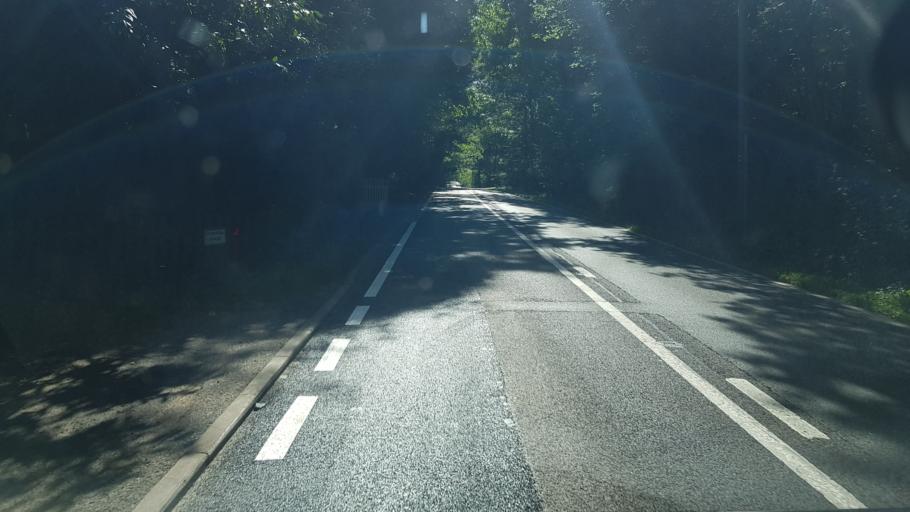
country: GB
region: England
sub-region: Kent
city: Kings Hill
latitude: 51.2776
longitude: 0.3538
